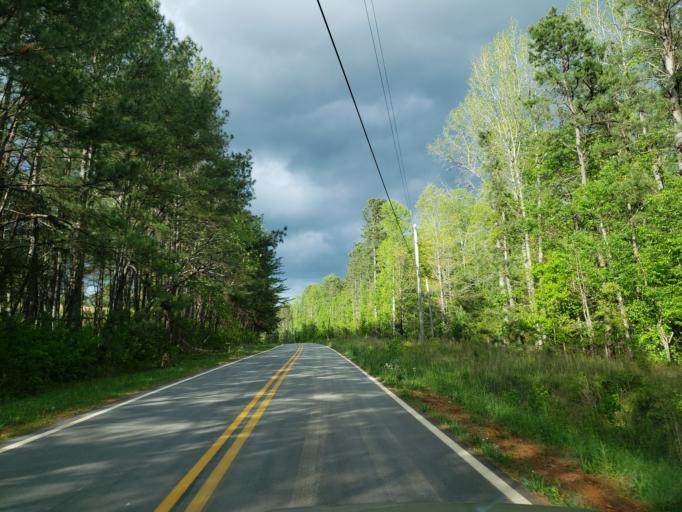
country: US
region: Georgia
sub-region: Haralson County
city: Tallapoosa
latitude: 33.8607
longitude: -85.3663
